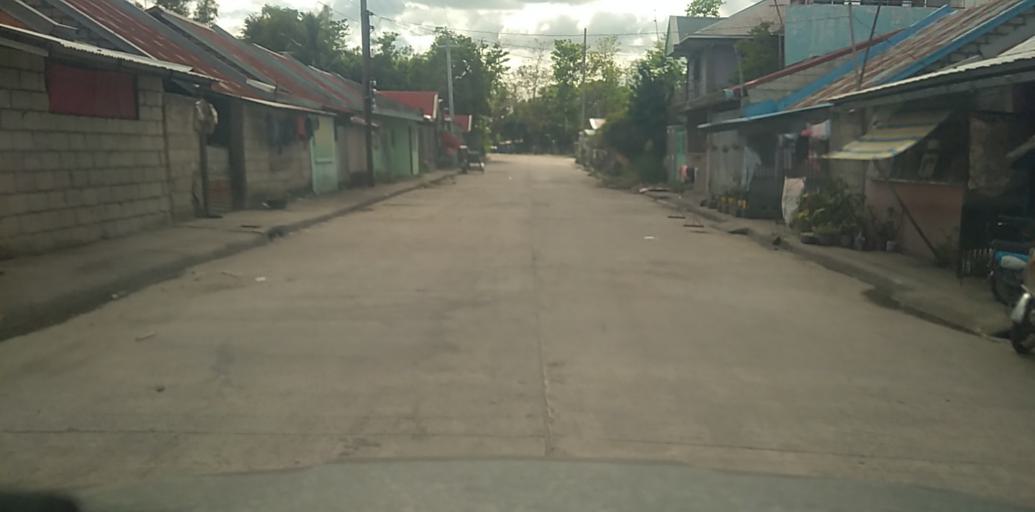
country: PH
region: Central Luzon
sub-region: Province of Pampanga
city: Pandacaqui
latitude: 15.1769
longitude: 120.6678
